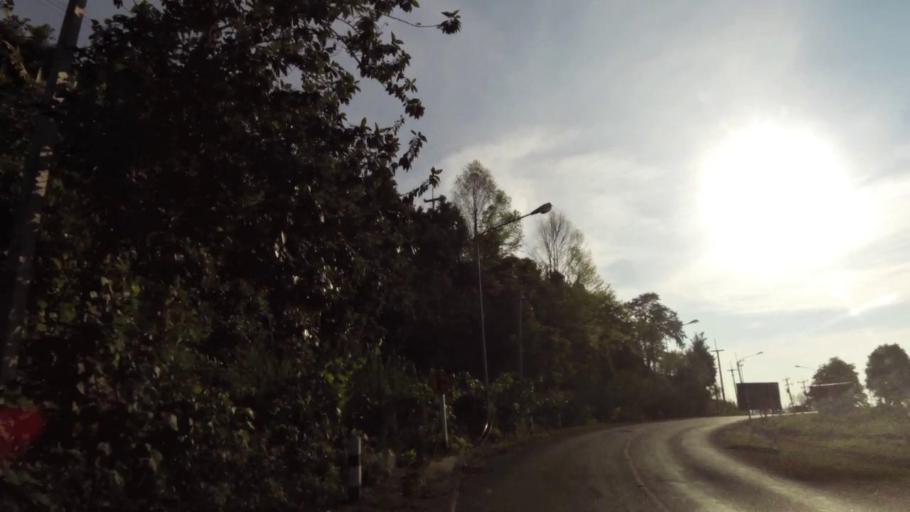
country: TH
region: Chiang Rai
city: Khun Tan
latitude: 19.8587
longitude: 100.4342
